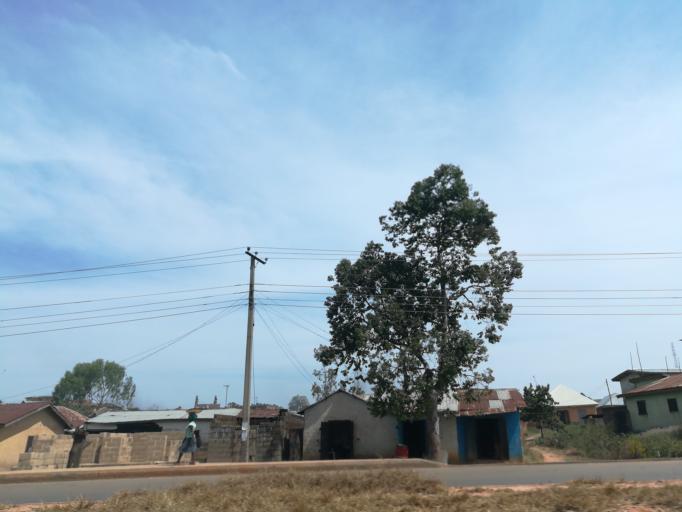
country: NG
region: Plateau
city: Bukuru
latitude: 9.7931
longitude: 8.8595
